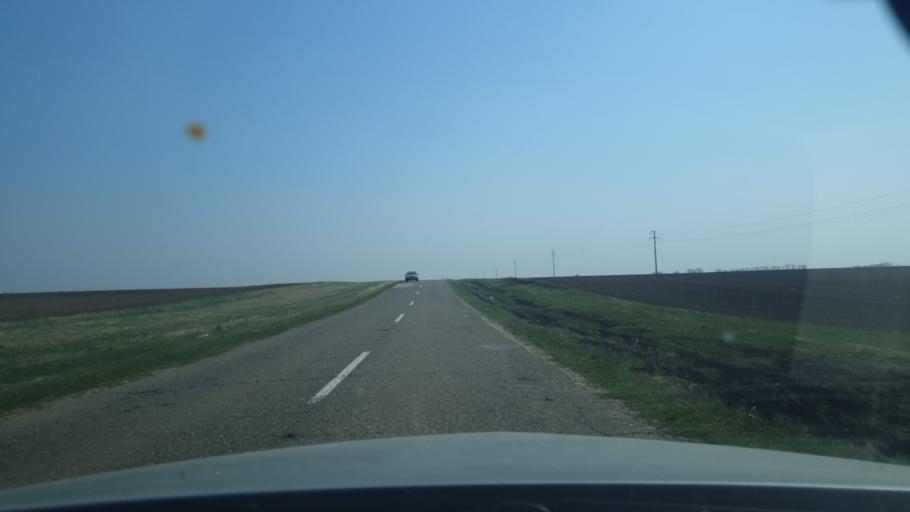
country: RS
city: Sasinci
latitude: 45.0308
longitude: 19.7509
